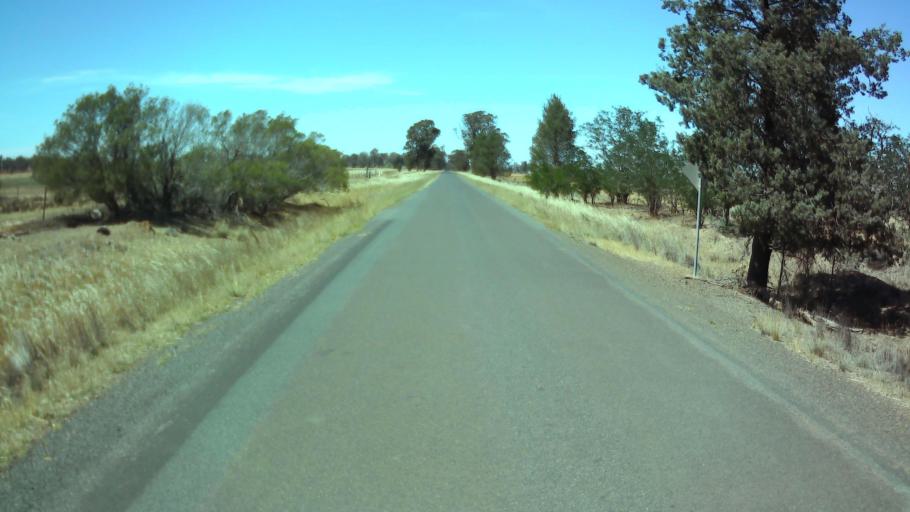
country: AU
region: New South Wales
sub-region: Weddin
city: Grenfell
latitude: -34.1033
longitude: 147.8872
